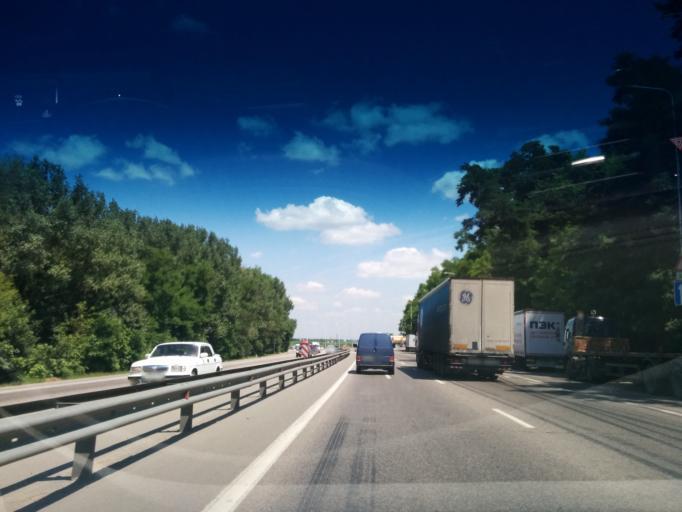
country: RU
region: Rostov
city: Aksay
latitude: 47.2979
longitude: 39.8602
